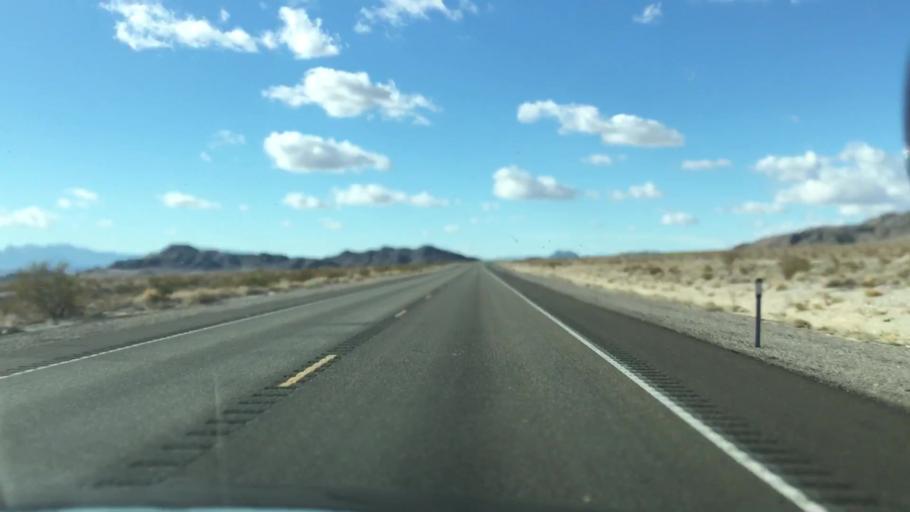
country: US
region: Nevada
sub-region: Nye County
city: Pahrump
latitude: 36.5720
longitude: -116.1744
